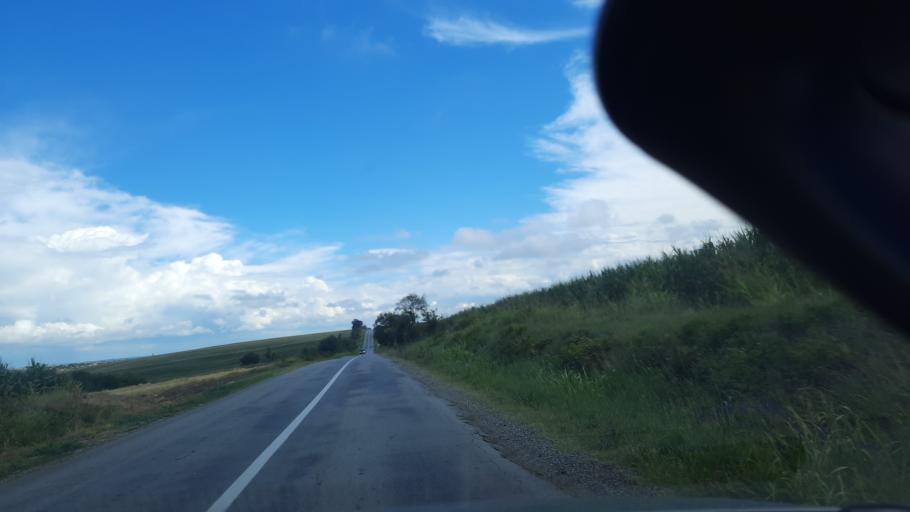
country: RS
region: Autonomna Pokrajina Vojvodina
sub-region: Sremski Okrug
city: Sremska Mitrovica
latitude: 45.0975
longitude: 19.5694
